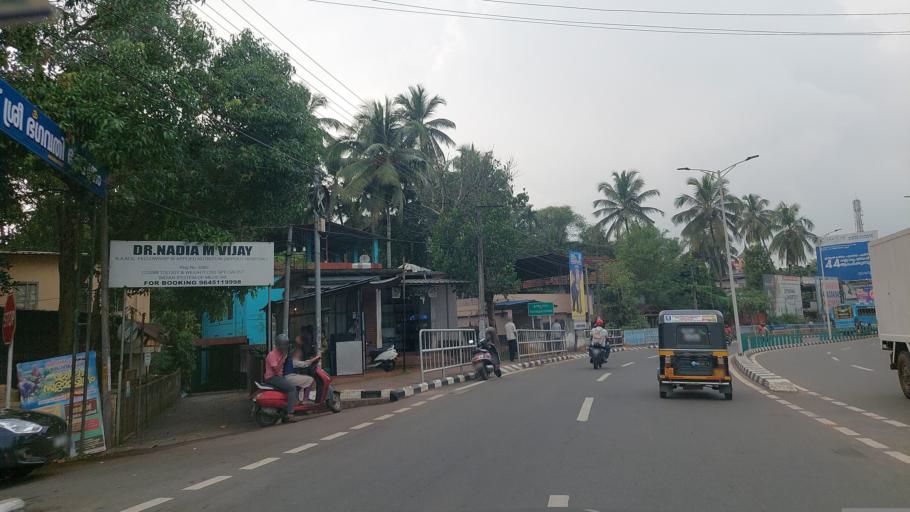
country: IN
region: Kerala
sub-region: Kozhikode
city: Kozhikode
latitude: 11.2859
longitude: 75.7824
